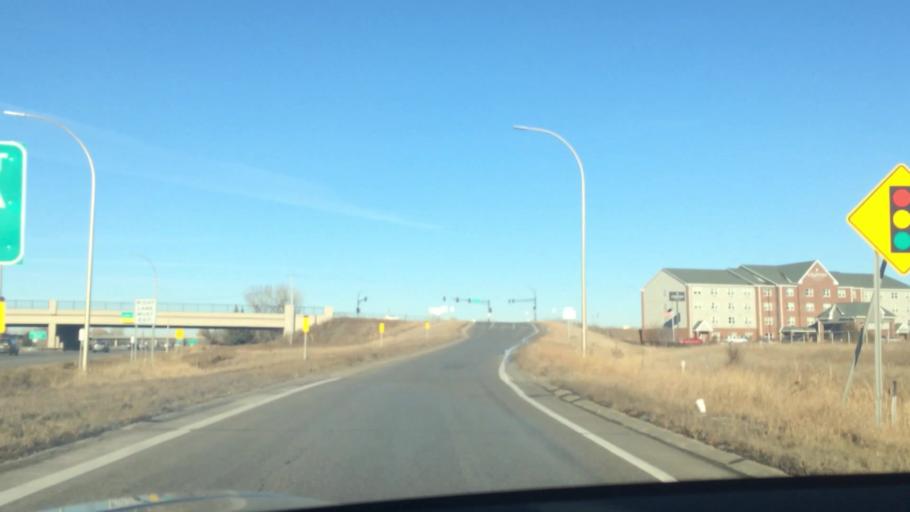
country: US
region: Minnesota
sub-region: Ramsey County
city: Mounds View
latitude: 45.1225
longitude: -93.1882
